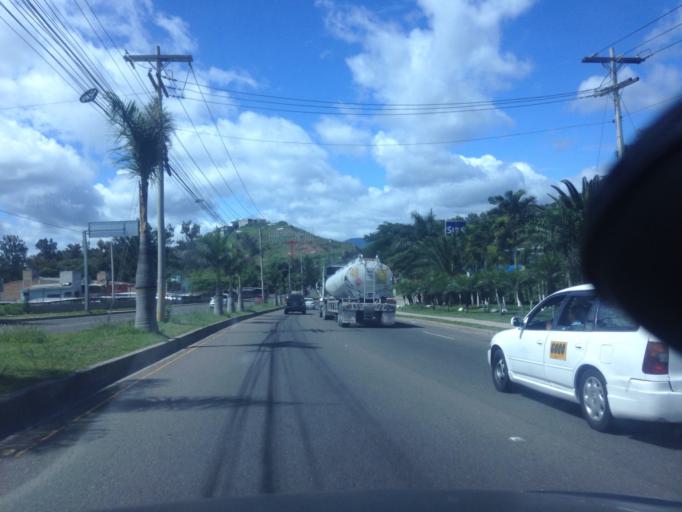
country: HN
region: Francisco Morazan
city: El Tablon
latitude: 14.0554
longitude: -87.1810
